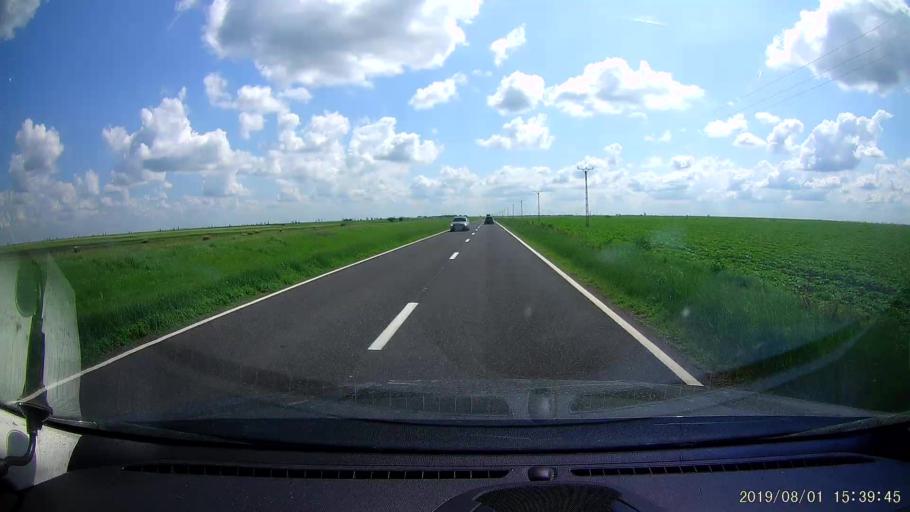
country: RO
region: Braila
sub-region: Comuna Baraganul
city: Baraganul
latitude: 44.8503
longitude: 27.5535
